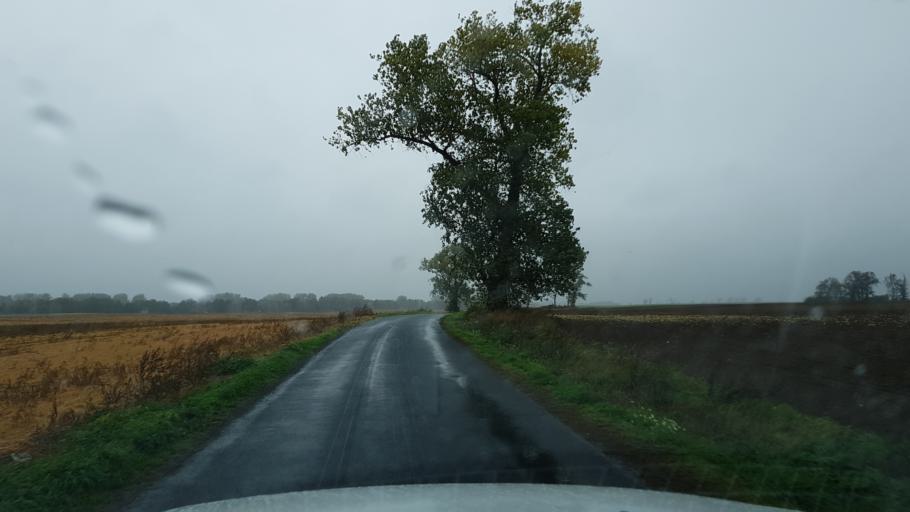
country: PL
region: West Pomeranian Voivodeship
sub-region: Powiat pyrzycki
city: Kozielice
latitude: 53.1731
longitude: 14.8155
